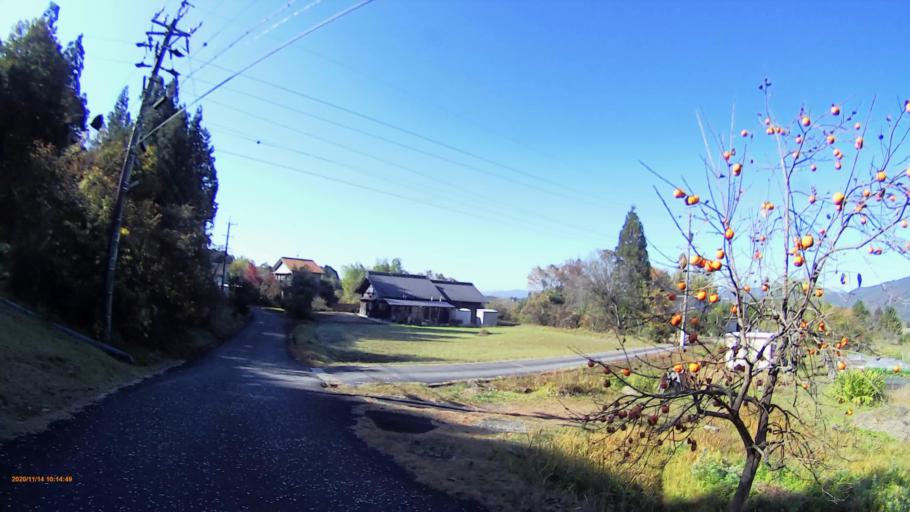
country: JP
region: Gifu
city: Nakatsugawa
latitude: 35.5120
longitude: 137.5416
